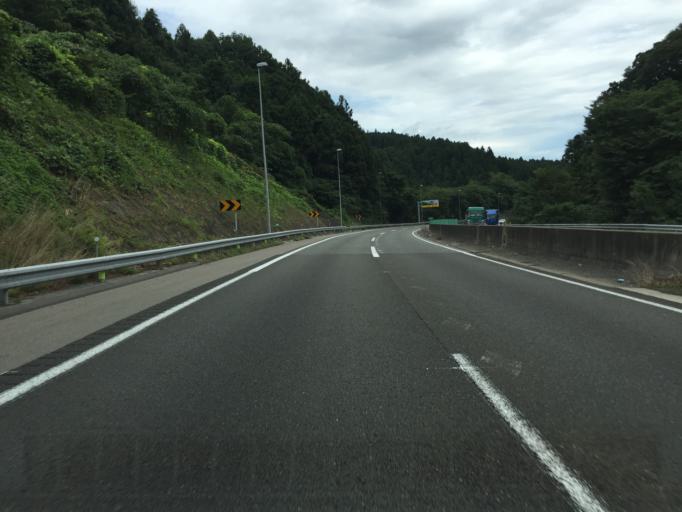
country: JP
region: Miyagi
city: Sendai
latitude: 38.1994
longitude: 140.7857
